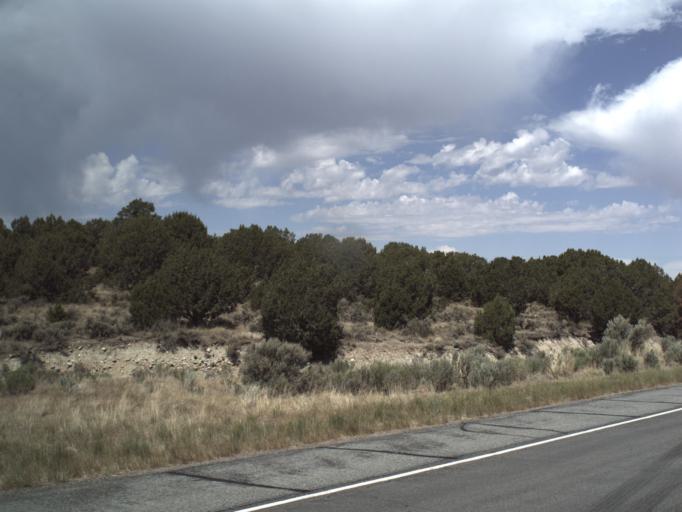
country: US
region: Utah
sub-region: Utah County
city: Eagle Mountain
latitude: 39.9848
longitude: -112.2631
